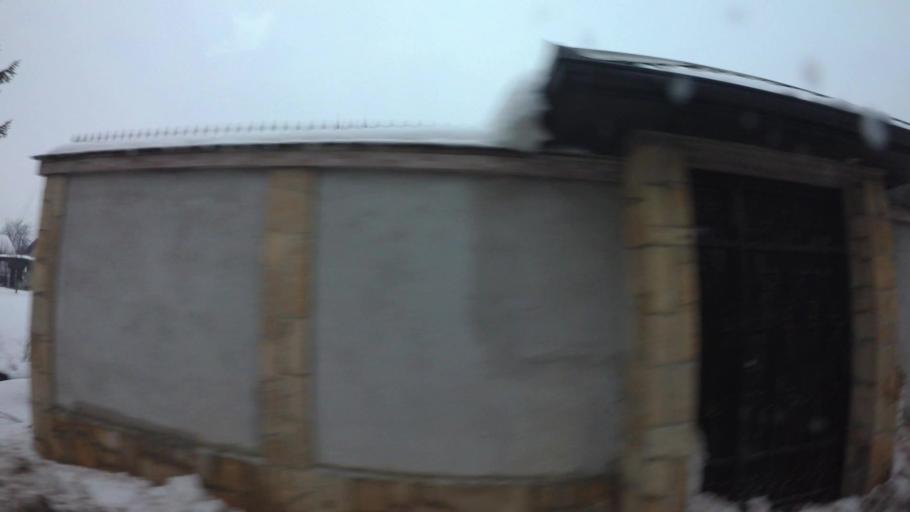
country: BA
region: Federation of Bosnia and Herzegovina
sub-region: Kanton Sarajevo
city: Sarajevo
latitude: 43.8440
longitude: 18.3034
